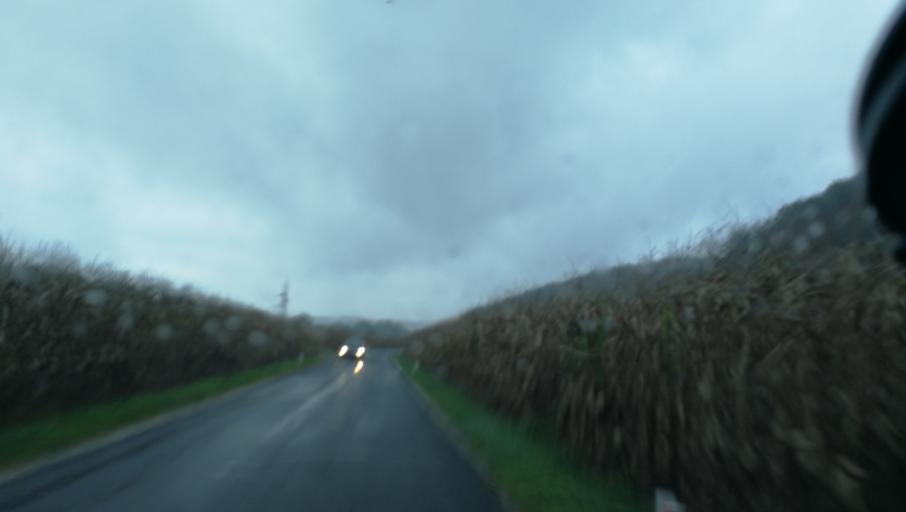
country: AT
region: Styria
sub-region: Politischer Bezirk Leibnitz
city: Strass in Steiermark
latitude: 46.7193
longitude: 15.6134
